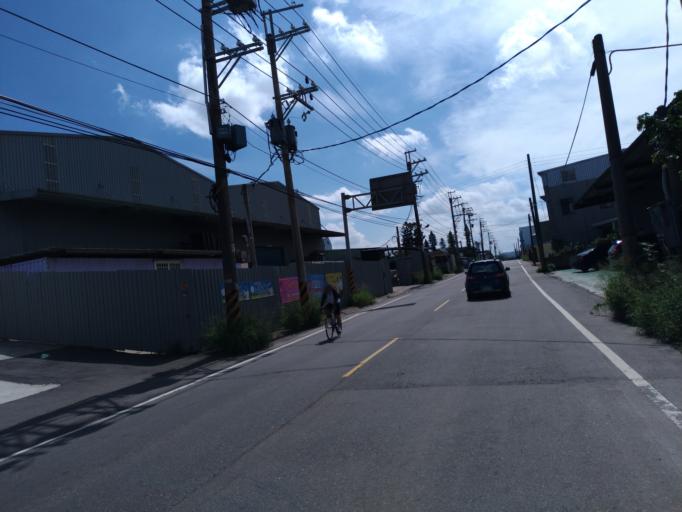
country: TW
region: Taiwan
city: Daxi
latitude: 24.9450
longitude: 121.1471
